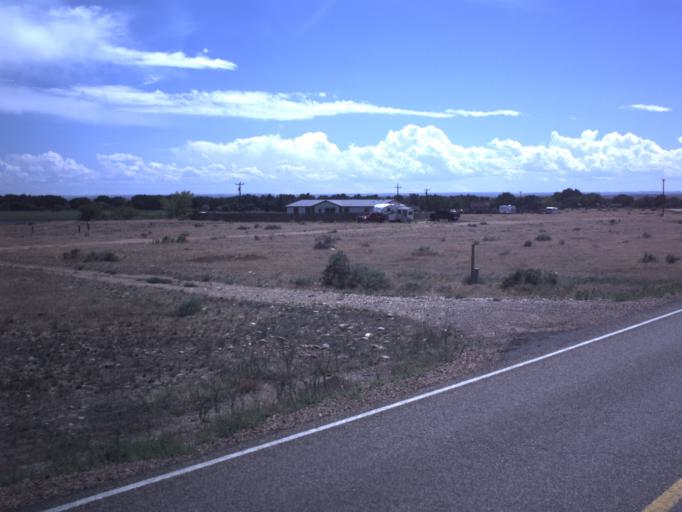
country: US
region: Utah
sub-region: Duchesne County
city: Roosevelt
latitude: 40.0958
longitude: -109.6799
